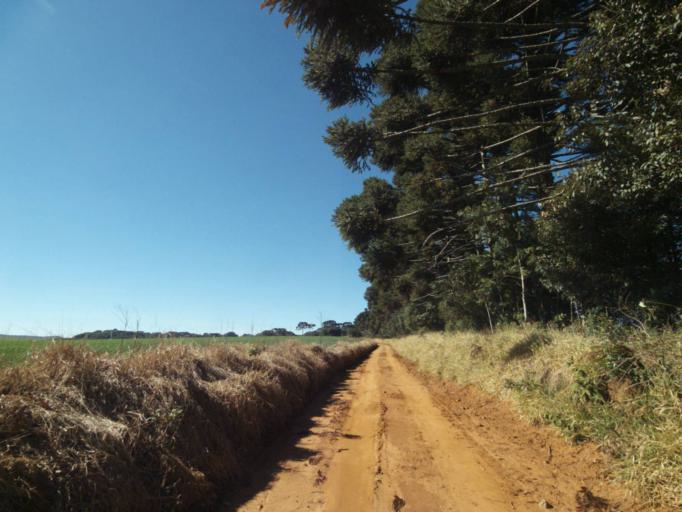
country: BR
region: Parana
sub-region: Tibagi
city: Tibagi
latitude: -24.5935
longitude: -50.2493
